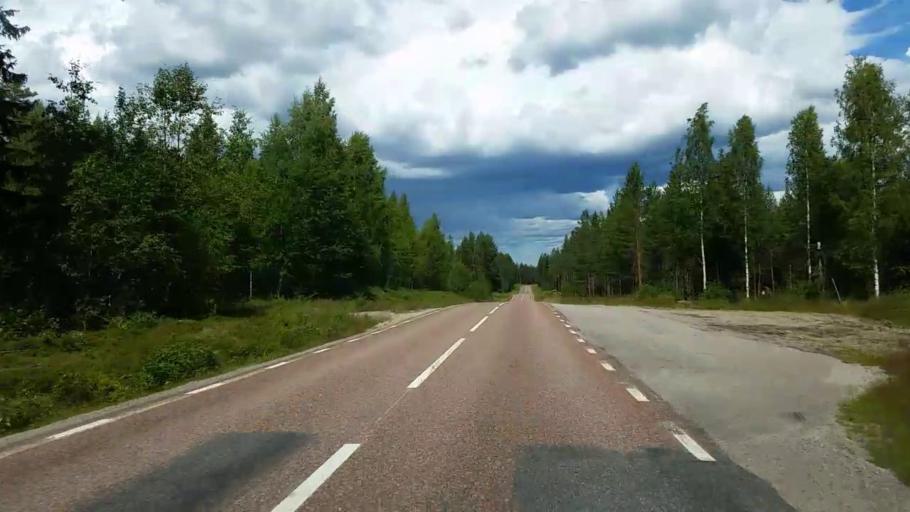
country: SE
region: Gaevleborg
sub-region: Ovanakers Kommun
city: Edsbyn
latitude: 61.3147
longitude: 15.5082
